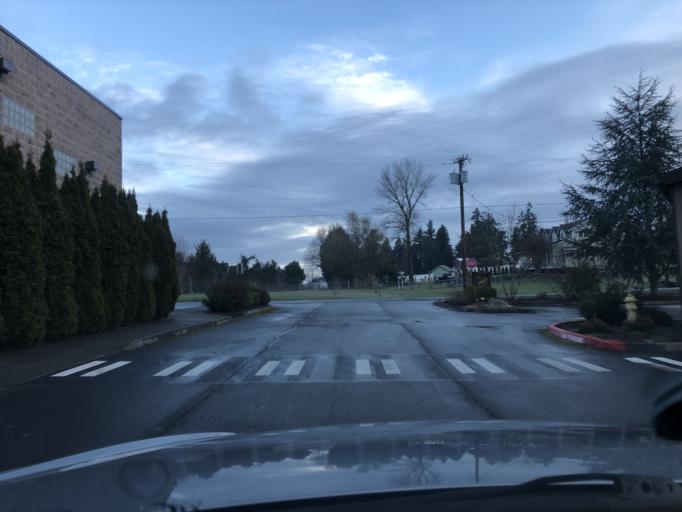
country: US
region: Washington
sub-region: Pierce County
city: North Puyallup
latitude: 47.2254
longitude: -122.2660
